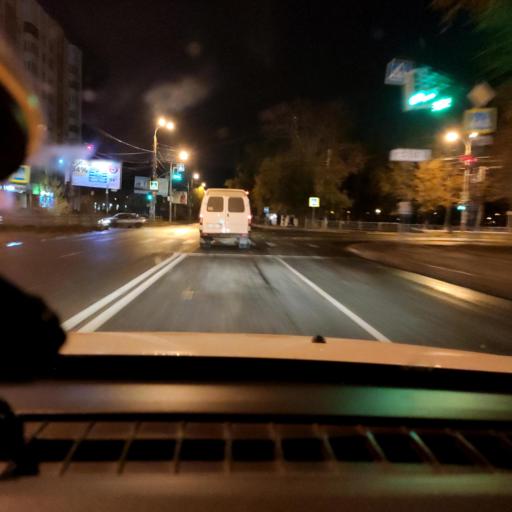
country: RU
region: Samara
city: Samara
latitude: 53.2246
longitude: 50.1989
